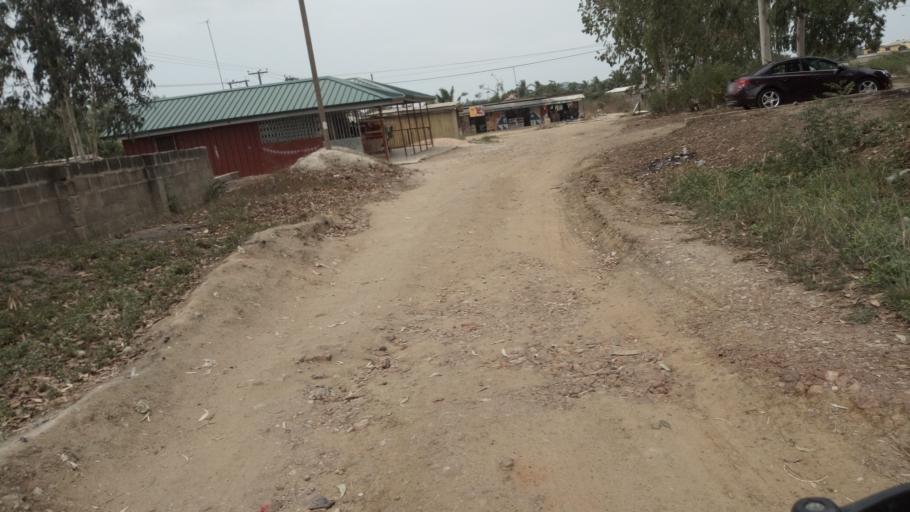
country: GH
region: Central
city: Winneba
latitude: 5.3668
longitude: -0.6381
